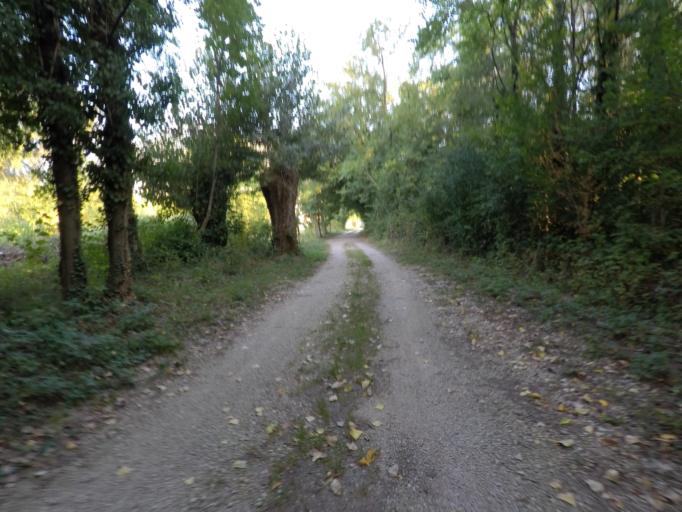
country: IT
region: Friuli Venezia Giulia
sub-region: Provincia di Udine
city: Trasaghis
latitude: 46.2790
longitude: 13.0767
